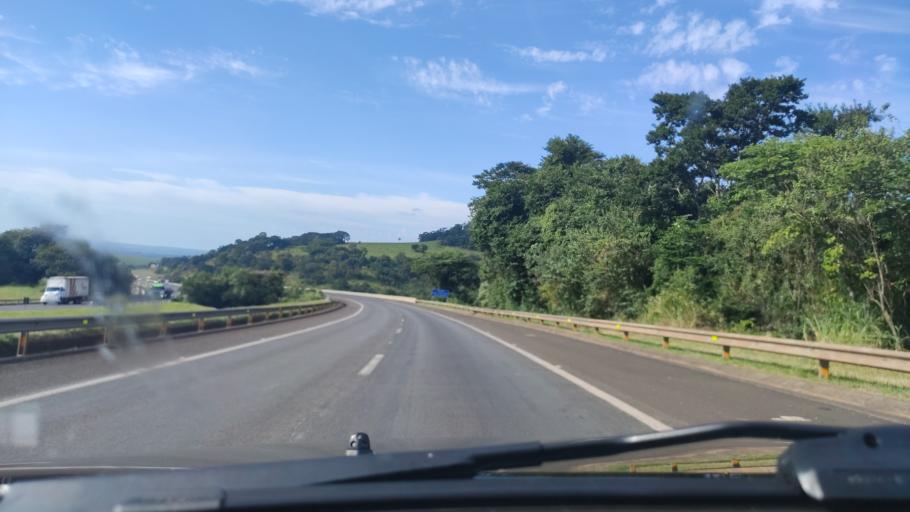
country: BR
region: Sao Paulo
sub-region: Itatinga
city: Itatinga
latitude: -23.1017
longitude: -48.5075
